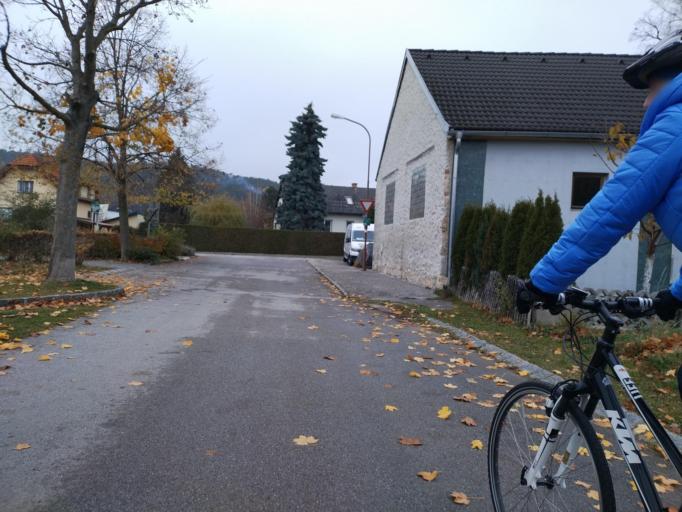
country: AT
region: Lower Austria
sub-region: Politischer Bezirk Neunkirchen
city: Pitten
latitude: 47.7130
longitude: 16.1785
